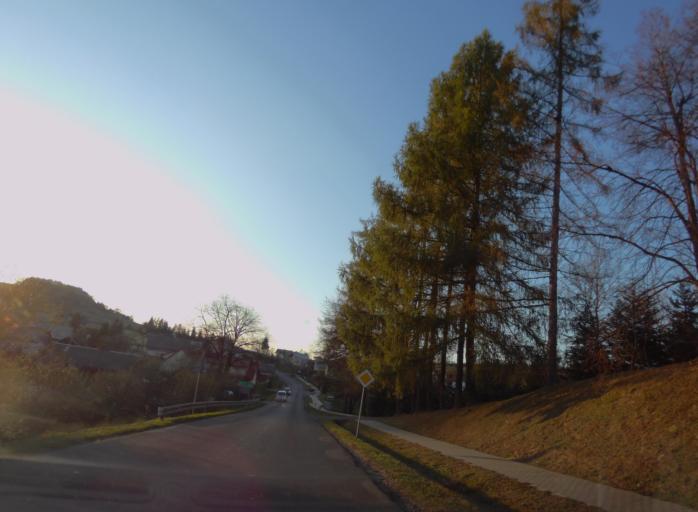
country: PL
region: Subcarpathian Voivodeship
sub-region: Powiat leski
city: Lesko
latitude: 49.4174
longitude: 22.3407
